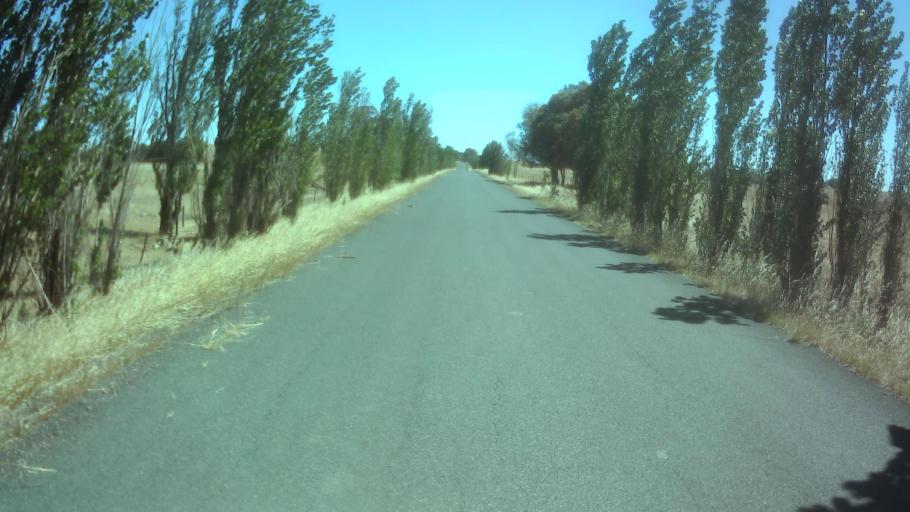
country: AU
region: New South Wales
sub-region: Weddin
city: Grenfell
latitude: -33.9748
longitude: 148.4038
